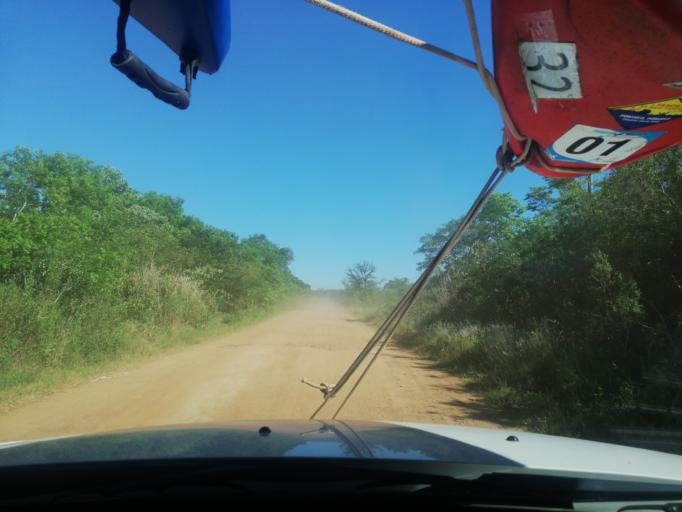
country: AR
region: Misiones
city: Santa Ana
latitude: -27.3322
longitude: -55.5848
